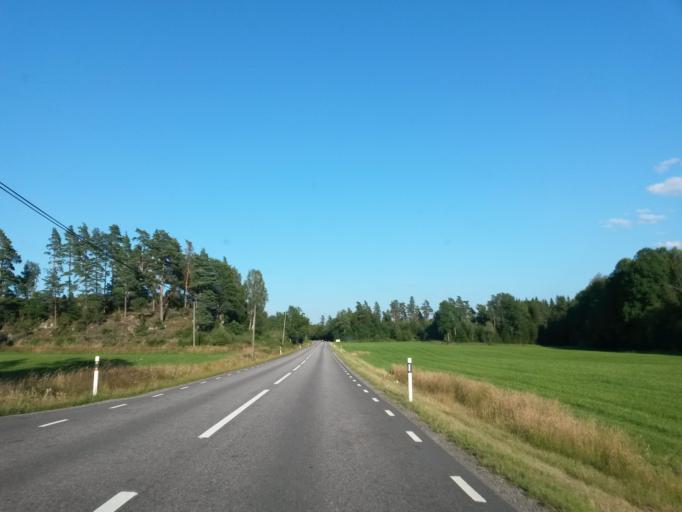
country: SE
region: Vaestra Goetaland
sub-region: Vargarda Kommun
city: Jonstorp
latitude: 58.0622
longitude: 12.6978
